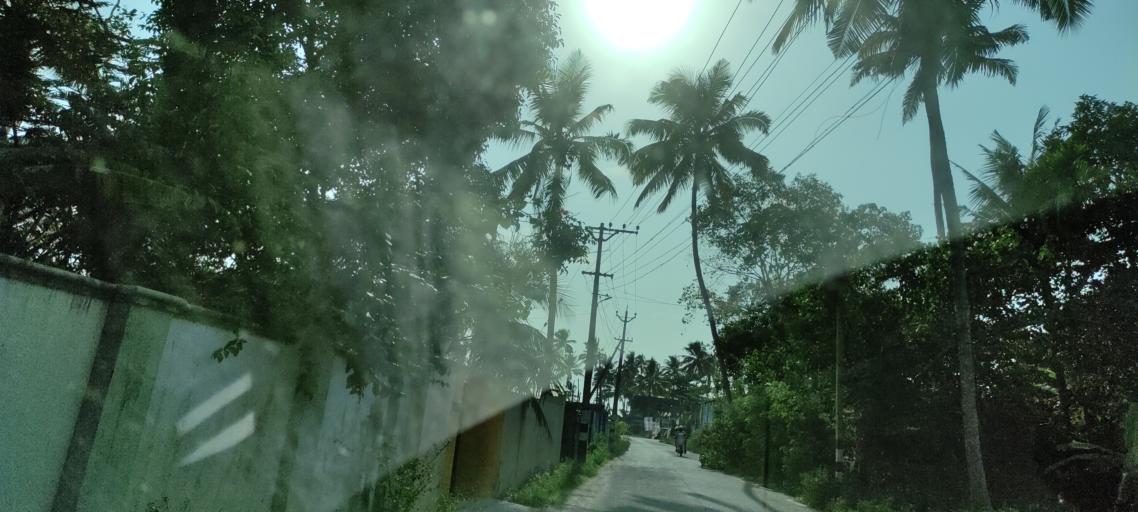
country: IN
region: Kerala
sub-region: Alappuzha
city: Vayalar
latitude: 9.6859
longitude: 76.2919
